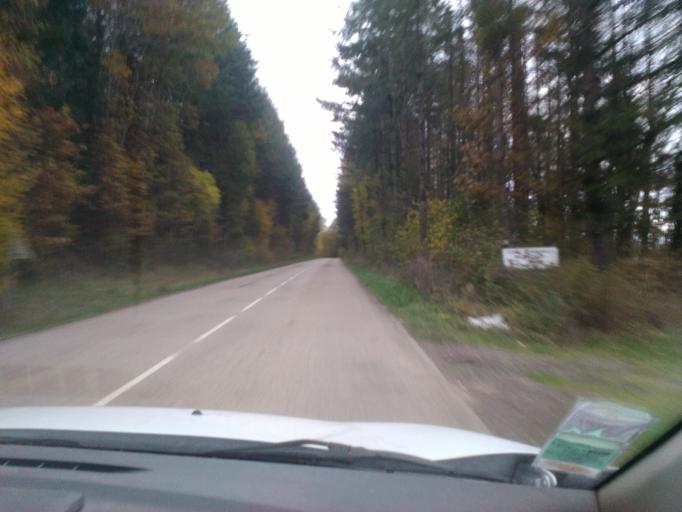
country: FR
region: Lorraine
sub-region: Departement des Vosges
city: Igney
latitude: 48.2519
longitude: 6.3539
